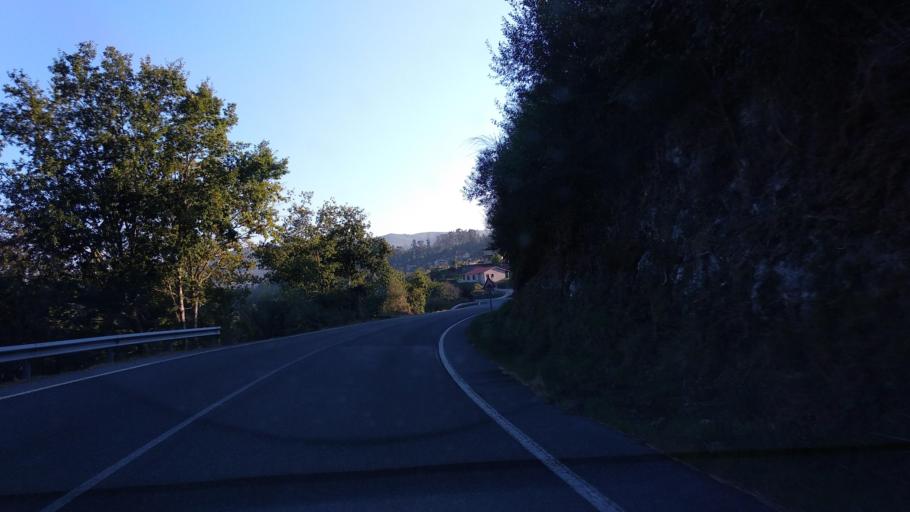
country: ES
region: Galicia
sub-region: Provincia de Pontevedra
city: Ponte Caldelas
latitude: 42.3573
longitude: -8.5414
